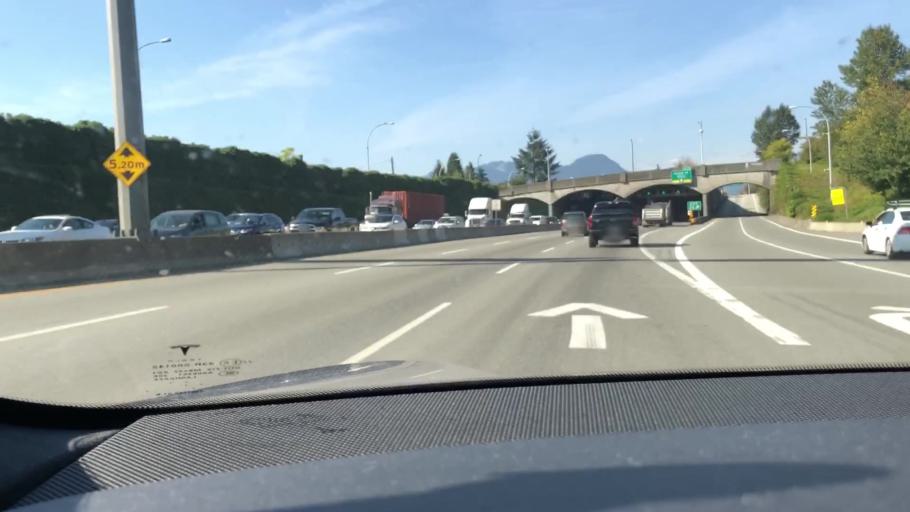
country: CA
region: British Columbia
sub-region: Fraser Valley Regional District
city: North Vancouver
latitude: 49.2759
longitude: -123.0313
